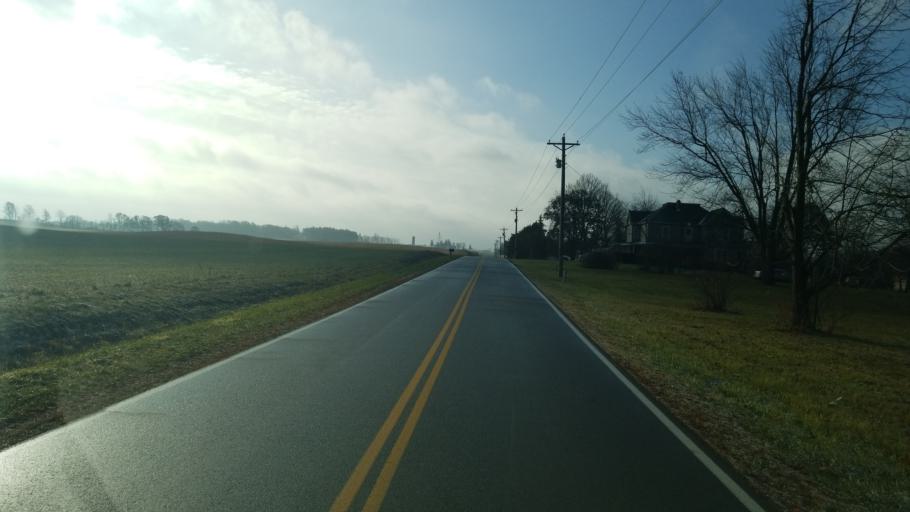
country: US
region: Ohio
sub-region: Richland County
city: Shelby
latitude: 40.9156
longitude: -82.7434
